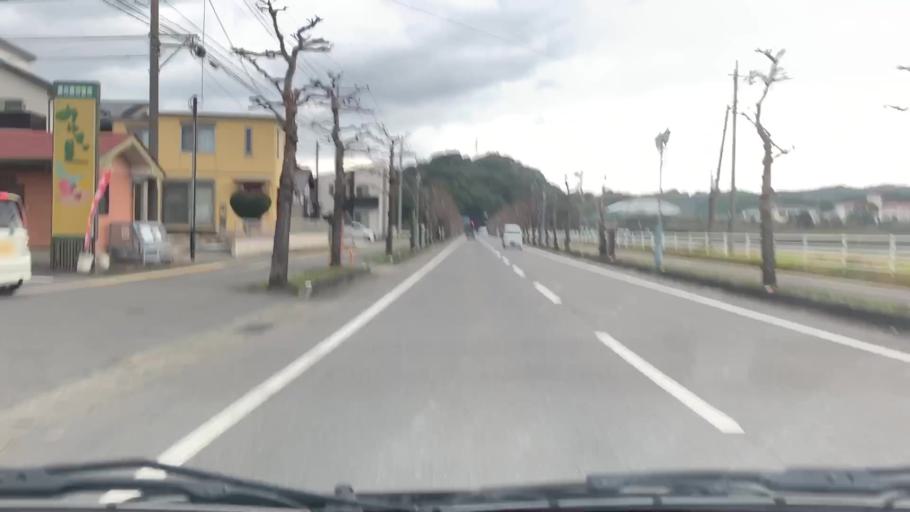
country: JP
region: Saga Prefecture
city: Ureshinomachi-shimojuku
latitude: 33.1045
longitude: 129.9854
